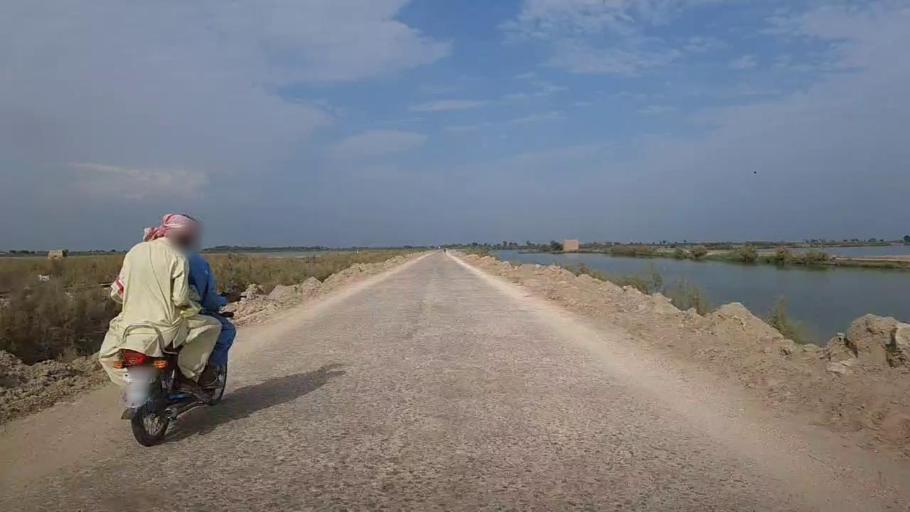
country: PK
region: Sindh
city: Thul
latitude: 28.2736
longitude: 68.8403
